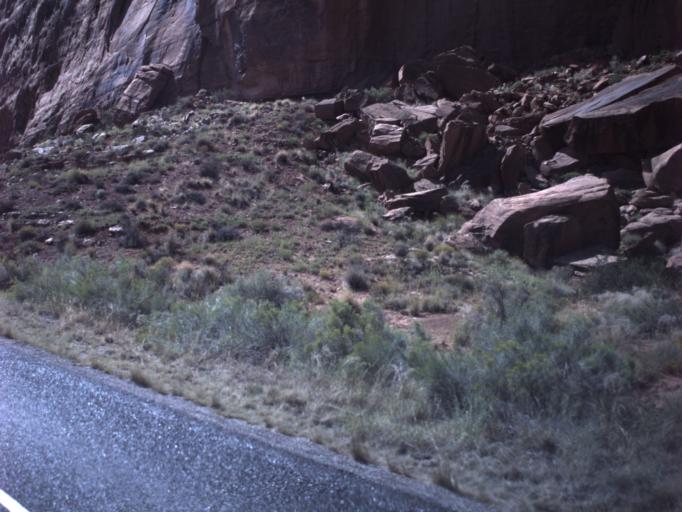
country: US
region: Utah
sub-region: Grand County
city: Moab
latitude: 38.6550
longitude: -109.7168
